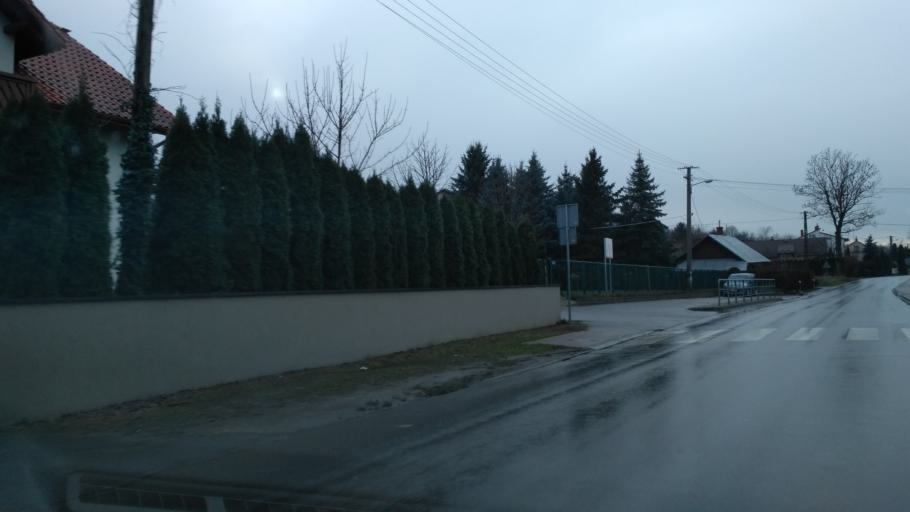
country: PL
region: Subcarpathian Voivodeship
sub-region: Powiat rzeszowski
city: Siedliska
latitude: 49.9527
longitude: 21.9455
